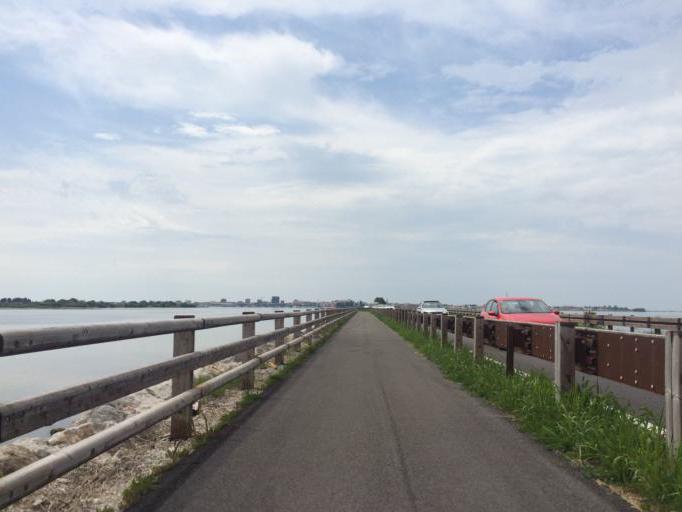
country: IT
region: Friuli Venezia Giulia
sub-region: Provincia di Gorizia
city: Grado
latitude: 45.7005
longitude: 13.3832
